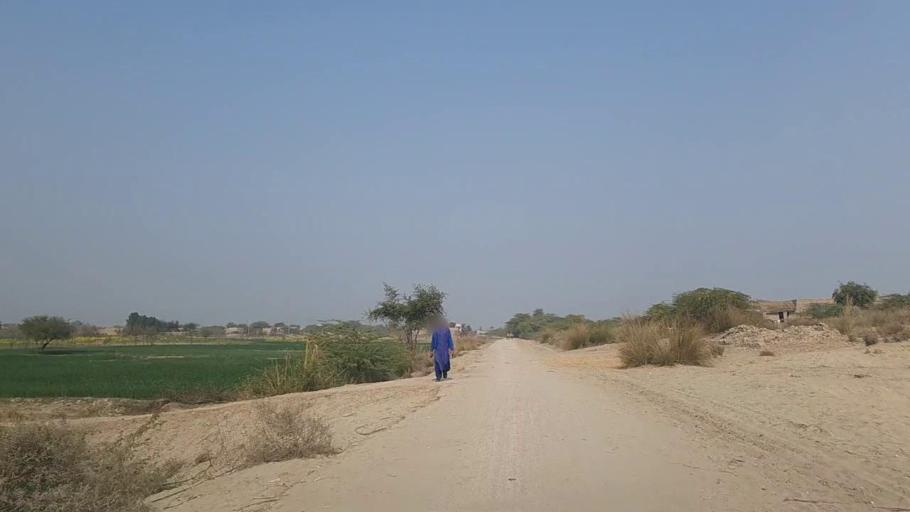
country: PK
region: Sindh
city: Daur
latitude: 26.4393
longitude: 68.4428
